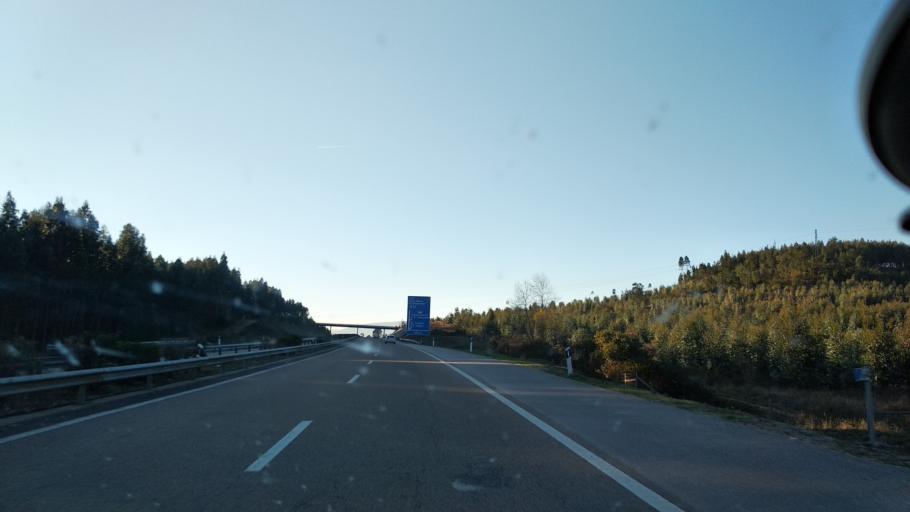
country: PT
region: Santarem
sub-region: Chamusca
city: Vila Nova da Barquinha
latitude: 39.4893
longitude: -8.4273
